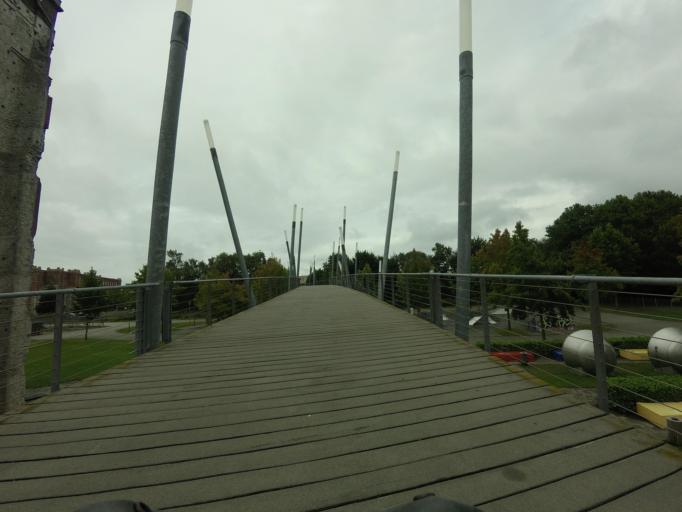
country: DE
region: North Rhine-Westphalia
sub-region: Regierungsbezirk Munster
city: Gronau
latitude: 52.2141
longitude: 7.0263
